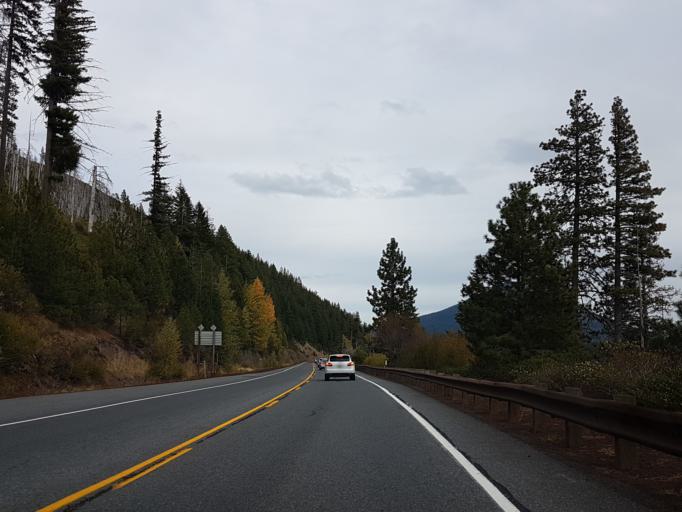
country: US
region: Oregon
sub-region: Deschutes County
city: Sisters
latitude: 44.4186
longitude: -121.7800
